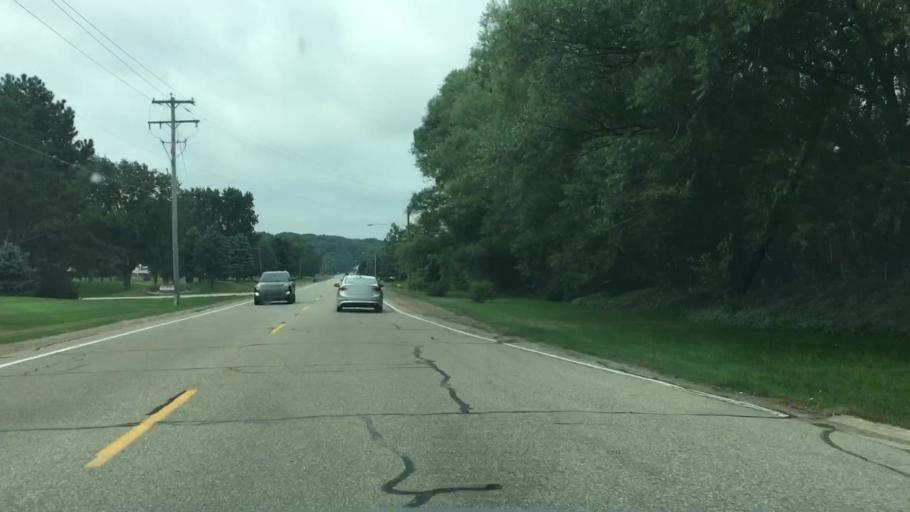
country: US
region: Michigan
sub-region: Ottawa County
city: Jenison
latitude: 42.8811
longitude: -85.8168
